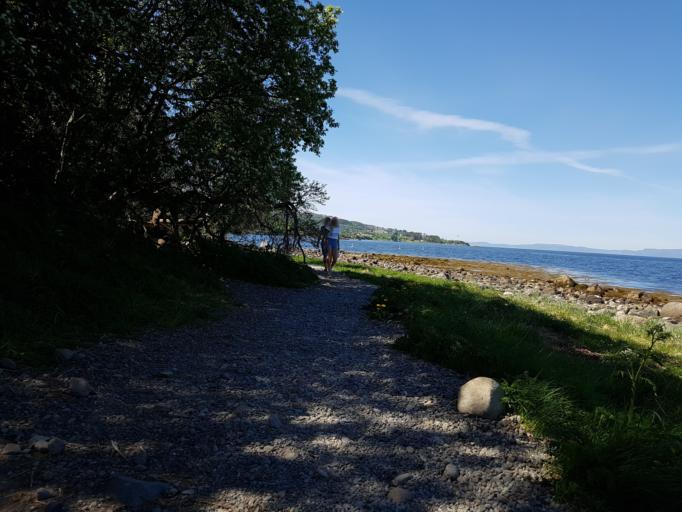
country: NO
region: Sor-Trondelag
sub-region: Malvik
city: Malvik
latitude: 63.4357
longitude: 10.7273
